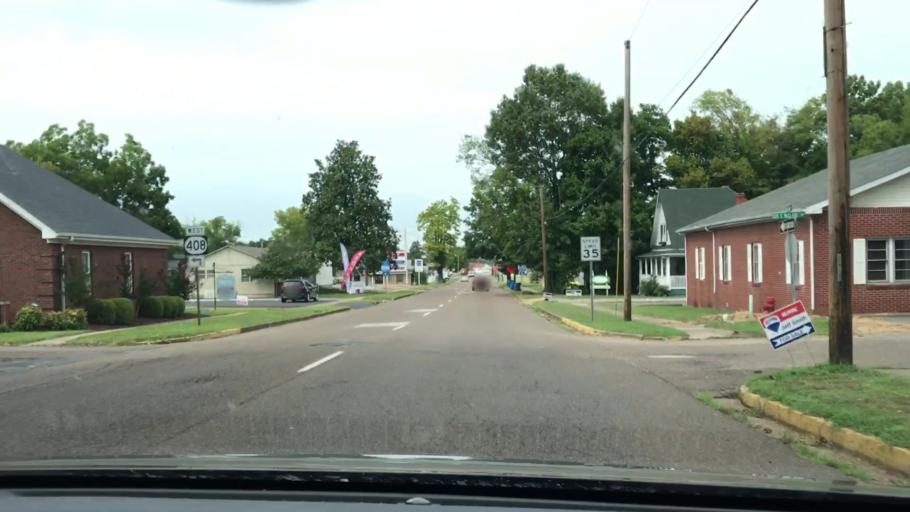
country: US
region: Kentucky
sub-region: Marshall County
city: Benton
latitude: 36.8600
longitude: -88.3499
